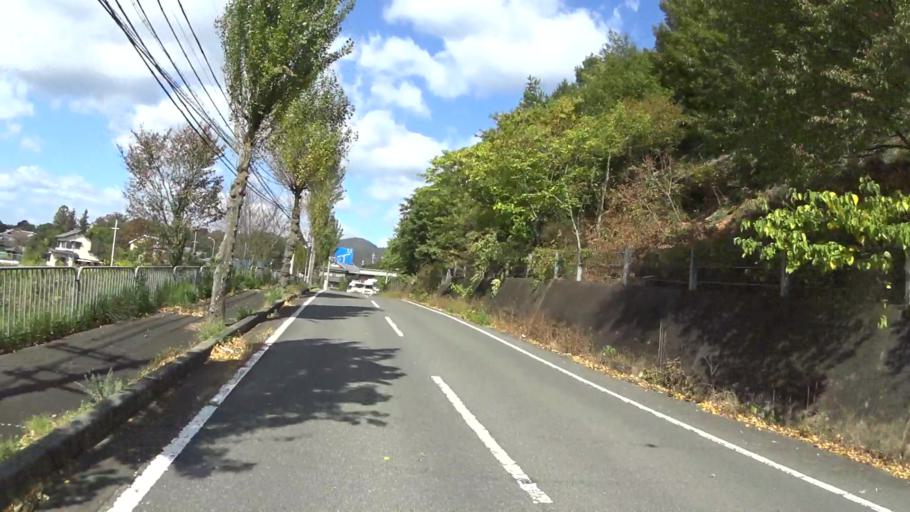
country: JP
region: Kyoto
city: Kameoka
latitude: 35.0821
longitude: 135.5659
